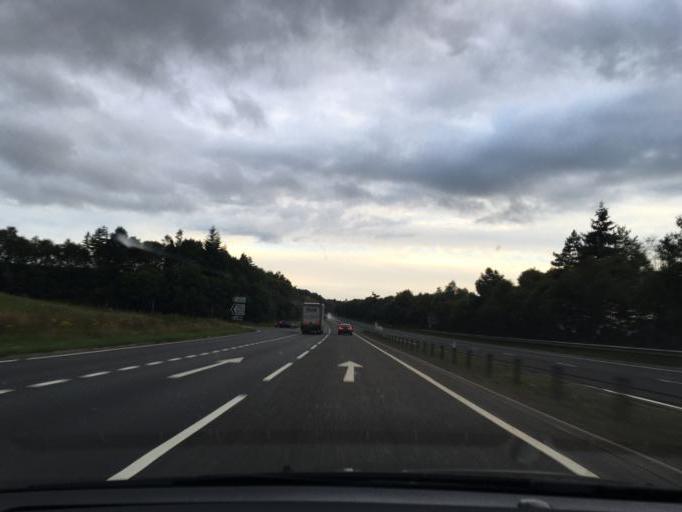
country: GB
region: Scotland
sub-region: Highland
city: Inverness
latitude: 57.4192
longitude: -4.1333
